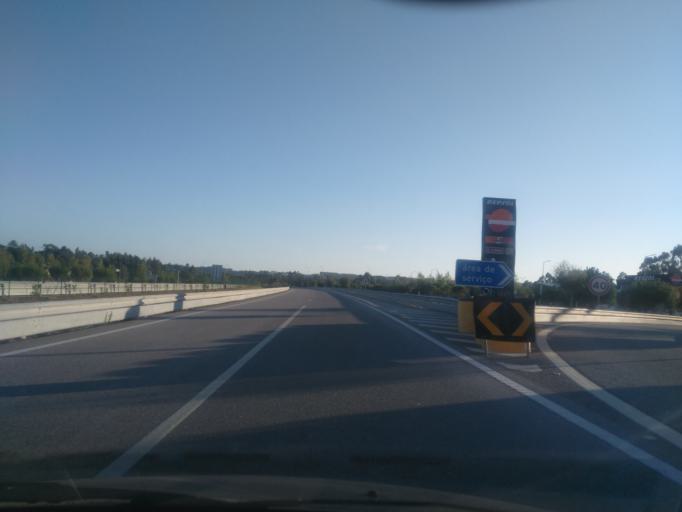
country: PT
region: Coimbra
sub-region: Figueira da Foz
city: Alhadas
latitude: 40.2139
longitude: -8.8098
